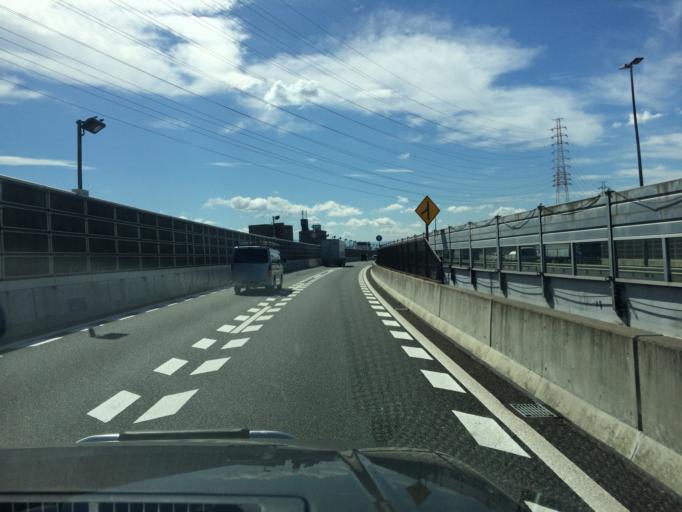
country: JP
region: Osaka
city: Daitocho
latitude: 34.7116
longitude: 135.5918
